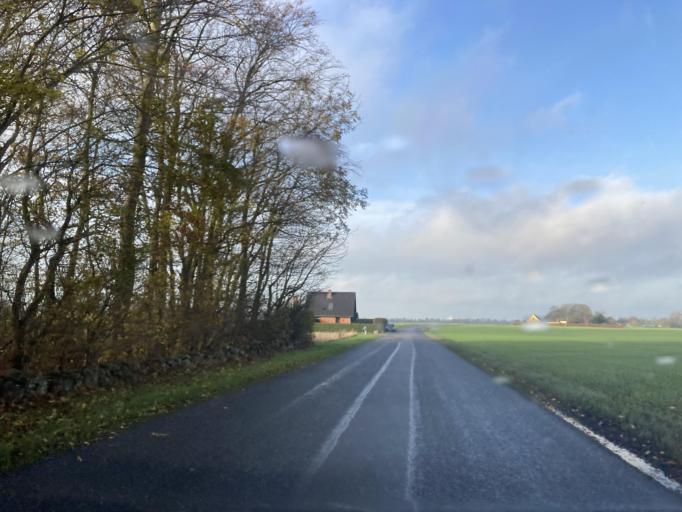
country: DK
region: Zealand
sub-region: Lolland Kommune
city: Rodby
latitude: 54.6812
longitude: 11.4132
